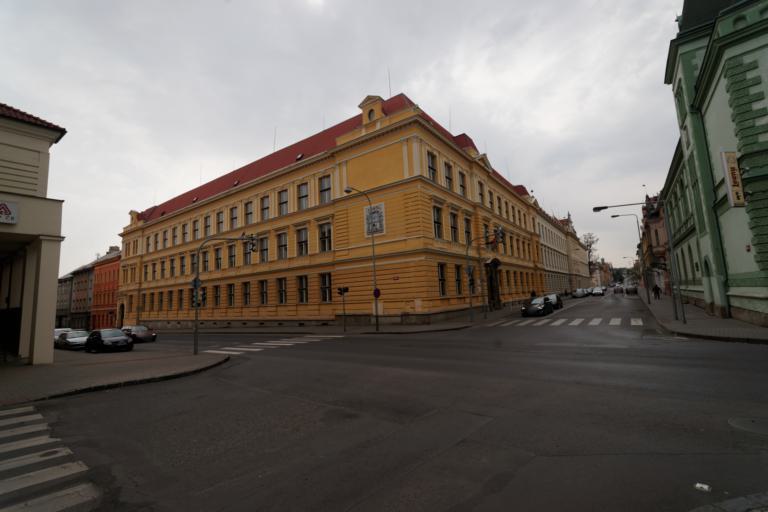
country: CZ
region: Ustecky
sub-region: Okres Louny
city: Louny
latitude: 50.3555
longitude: 13.7983
